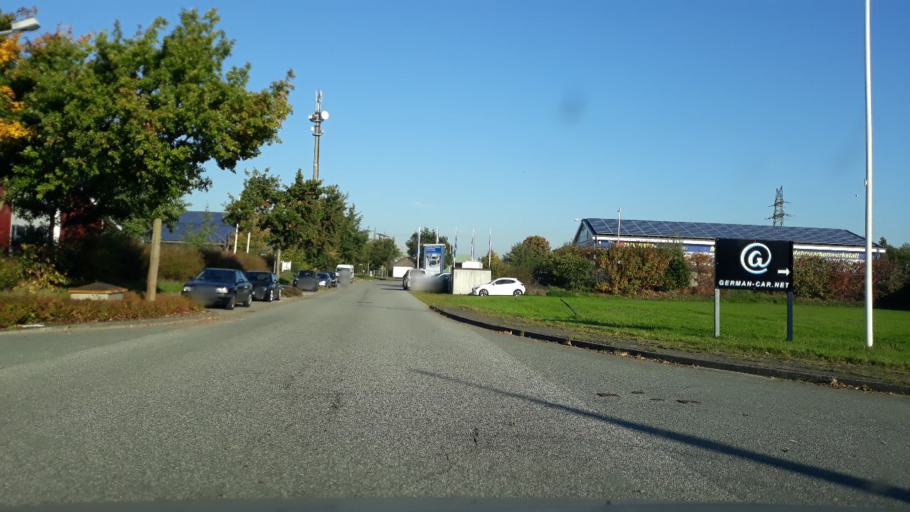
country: DE
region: Schleswig-Holstein
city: Kropp
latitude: 54.4144
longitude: 9.5281
